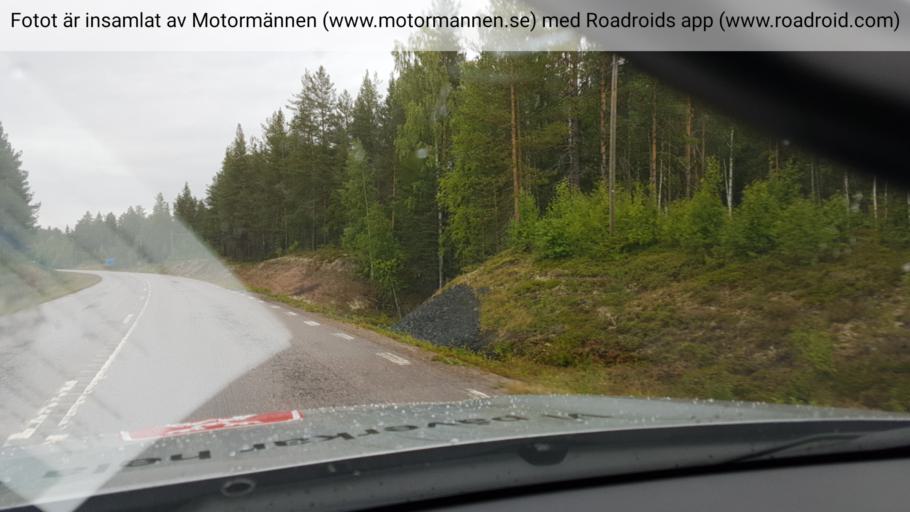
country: SE
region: Norrbotten
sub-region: Alvsbyns Kommun
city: AElvsbyn
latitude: 66.2258
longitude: 20.8754
